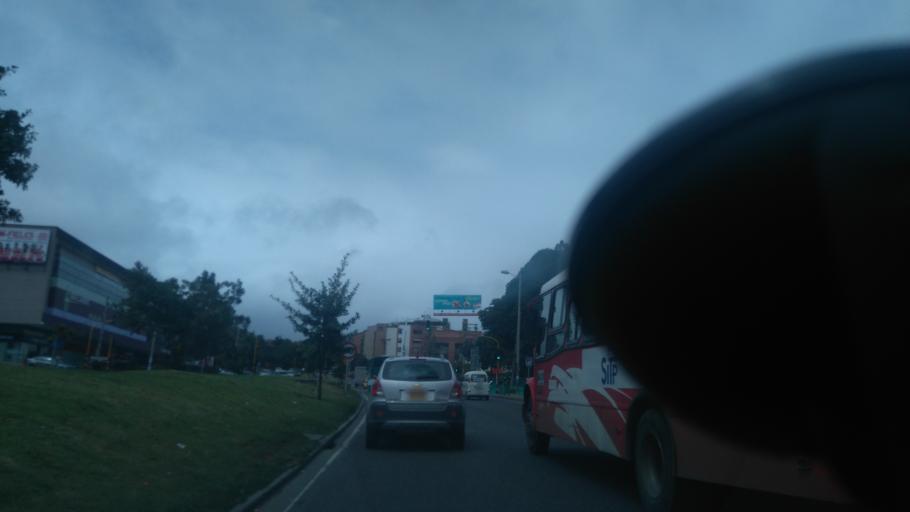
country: CO
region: Cundinamarca
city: La Calera
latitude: 4.7284
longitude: -74.0244
